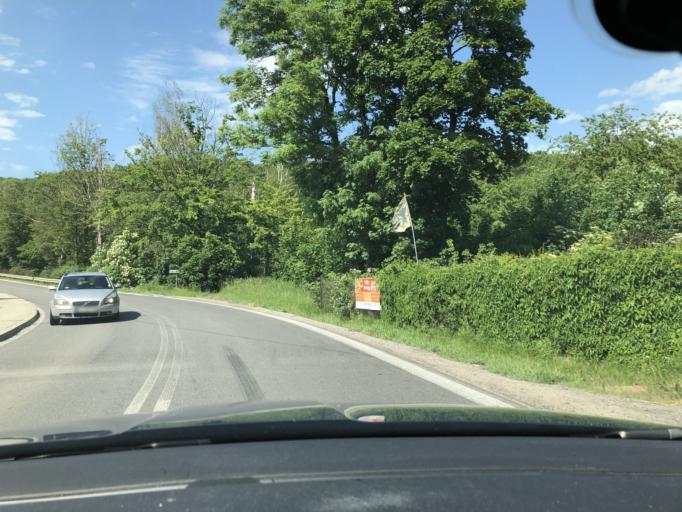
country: PL
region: Lower Silesian Voivodeship
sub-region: Powiat jaworski
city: Bolkow
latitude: 50.9343
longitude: 16.1142
